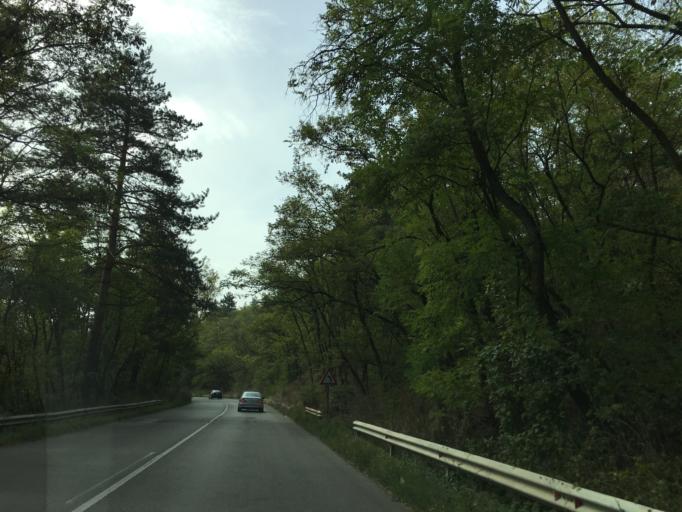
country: BG
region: Sofiya
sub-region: Obshtina Samokov
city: Samokov
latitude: 42.4507
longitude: 23.5542
